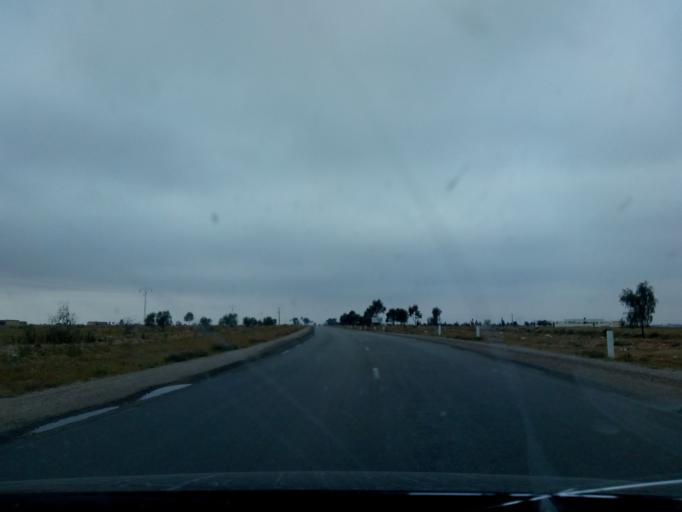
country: TN
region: Madanin
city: Medenine
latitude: 33.2794
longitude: 10.4694
